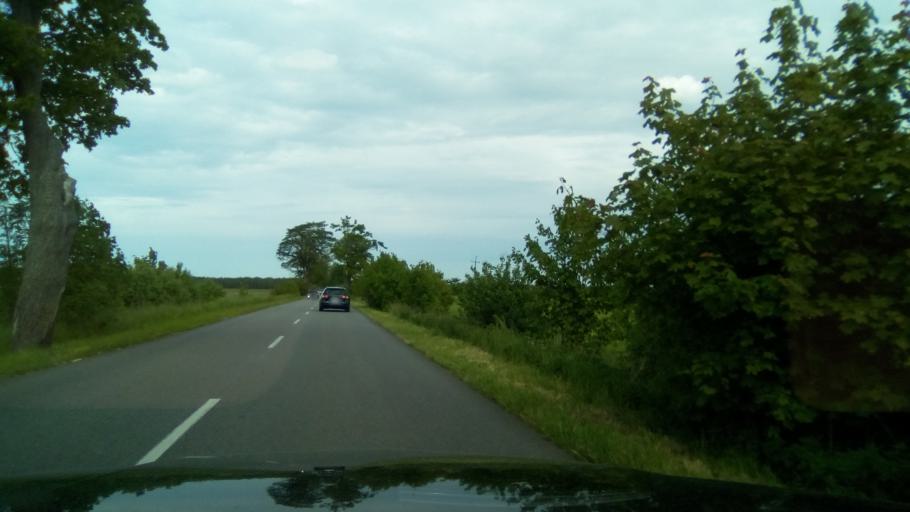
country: PL
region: Pomeranian Voivodeship
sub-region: Powiat pucki
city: Wierzchucino
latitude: 54.7906
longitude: 18.0162
